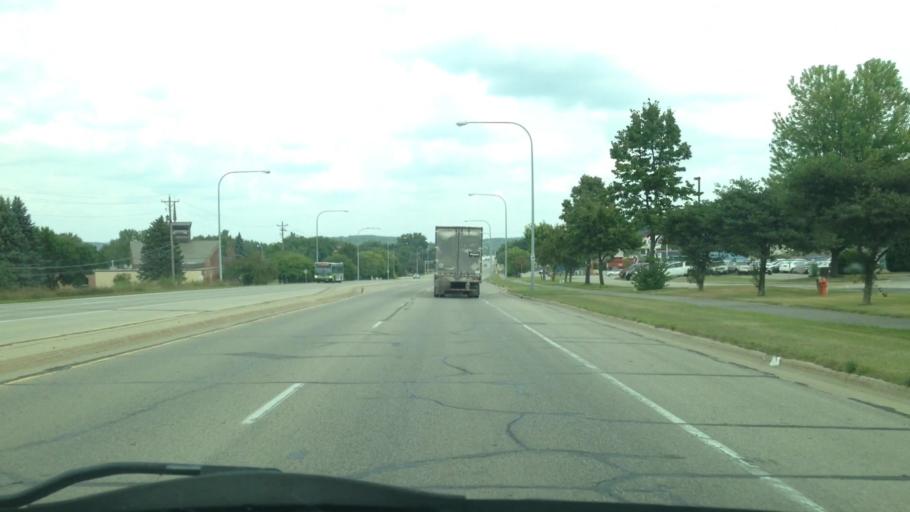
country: US
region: Minnesota
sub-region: Olmsted County
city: Rochester
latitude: 44.0505
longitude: -92.4555
